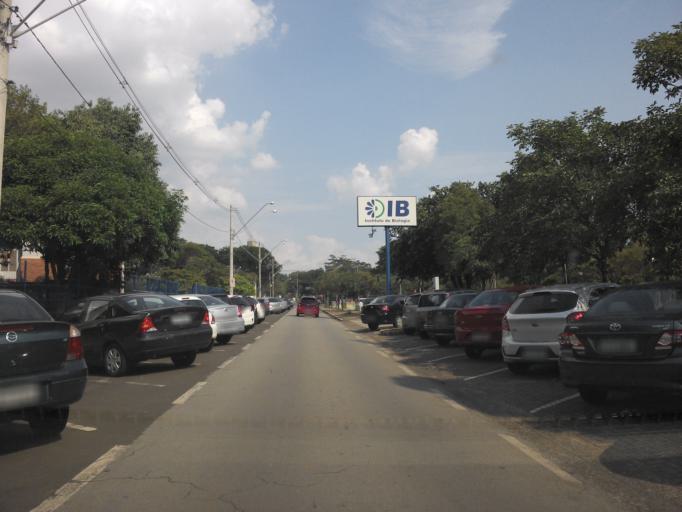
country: BR
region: Sao Paulo
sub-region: Campinas
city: Campinas
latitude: -22.8191
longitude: -47.0689
